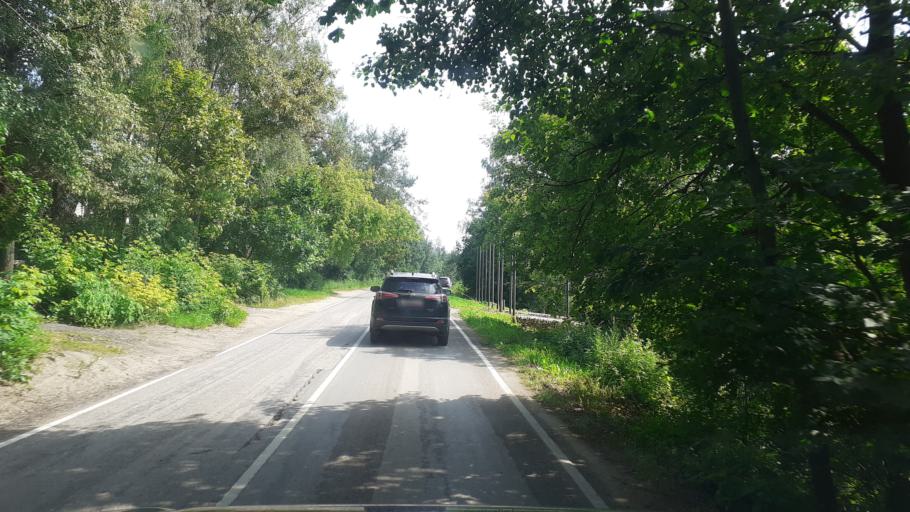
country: RU
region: Moskovskaya
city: Chupryakovo
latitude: 55.5800
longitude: 36.5694
